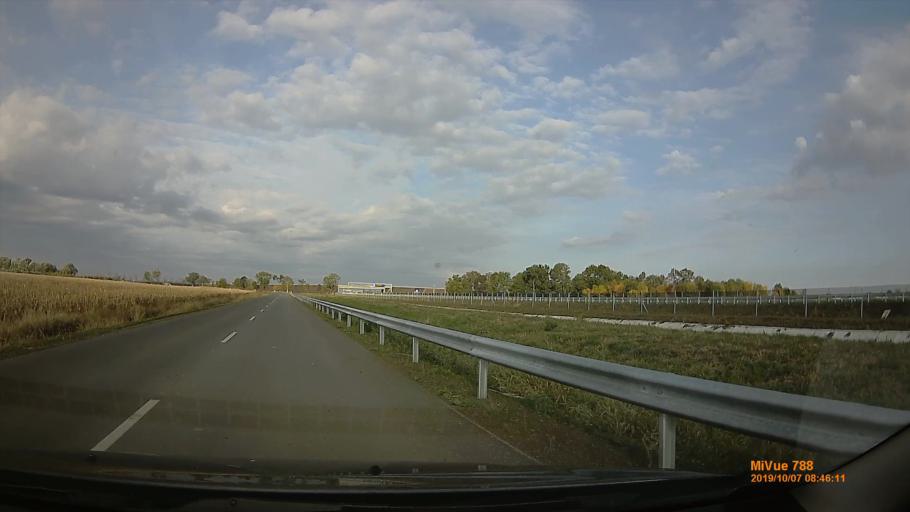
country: HU
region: Bekes
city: Szarvas
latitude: 46.8176
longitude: 20.5239
